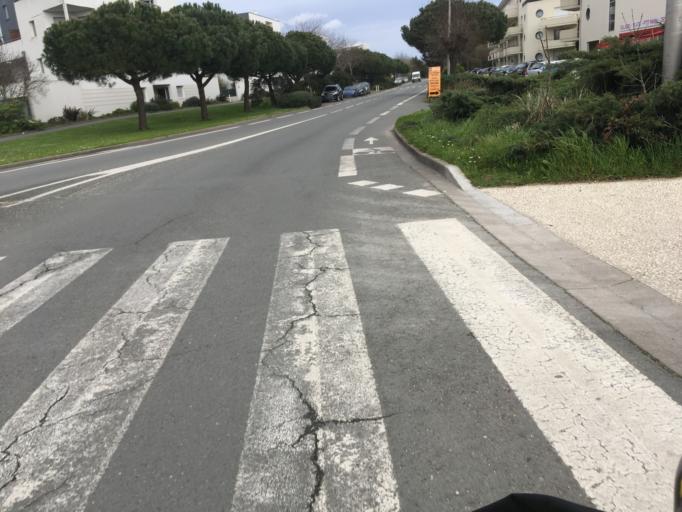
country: FR
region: Poitou-Charentes
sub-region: Departement de la Charente-Maritime
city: La Rochelle
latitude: 46.1420
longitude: -1.1570
